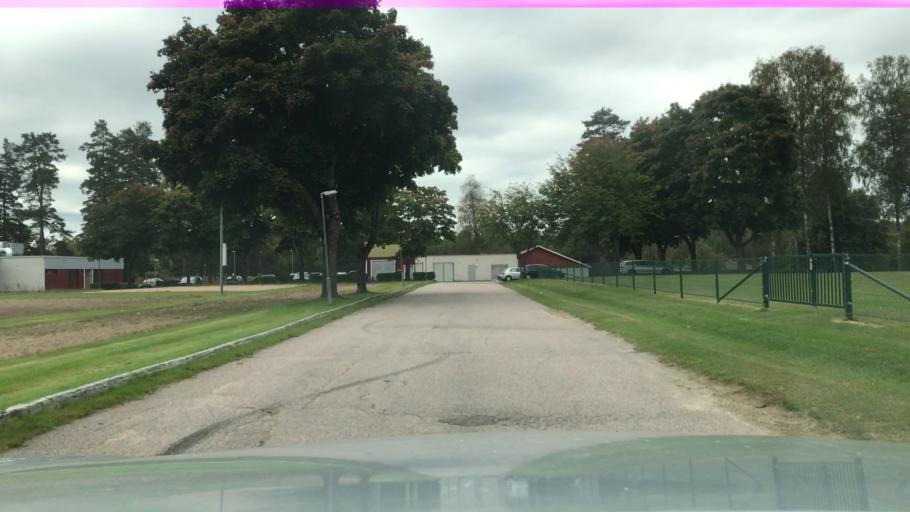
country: SE
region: Vaermland
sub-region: Munkfors Kommun
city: Munkfors
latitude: 59.8382
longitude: 13.5345
